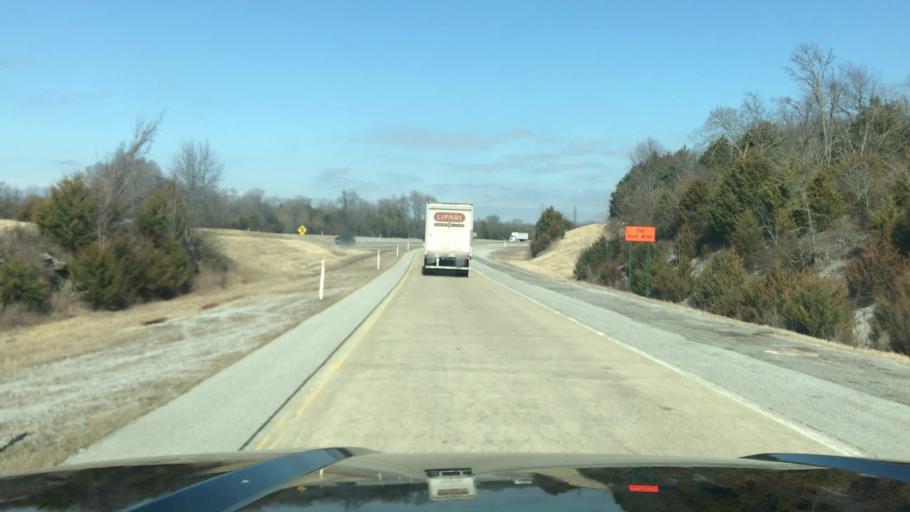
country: US
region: Tennessee
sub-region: Rutherford County
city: Smyrna
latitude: 35.9868
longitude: -86.4364
